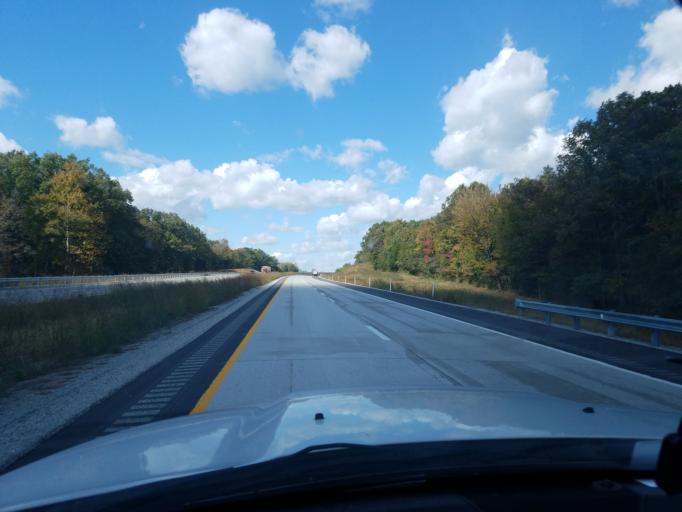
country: US
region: Kentucky
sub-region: Ohio County
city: Oak Grove
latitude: 37.3476
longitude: -86.7796
